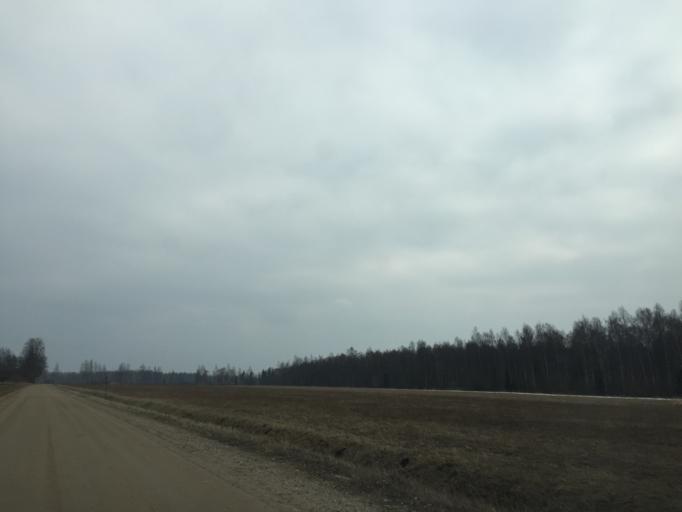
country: LV
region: Salacgrivas
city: Ainazi
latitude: 58.0304
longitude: 24.4715
